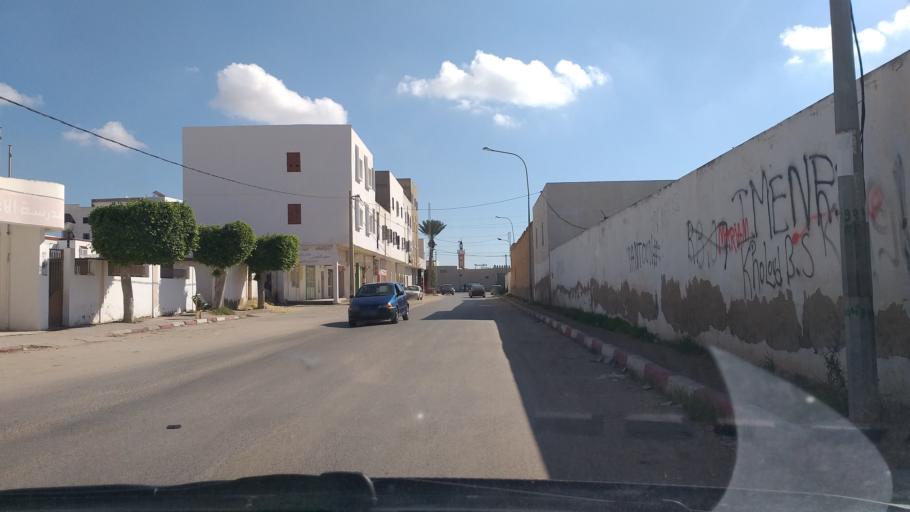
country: TN
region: Safaqis
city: Al Qarmadah
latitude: 34.7990
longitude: 10.7816
